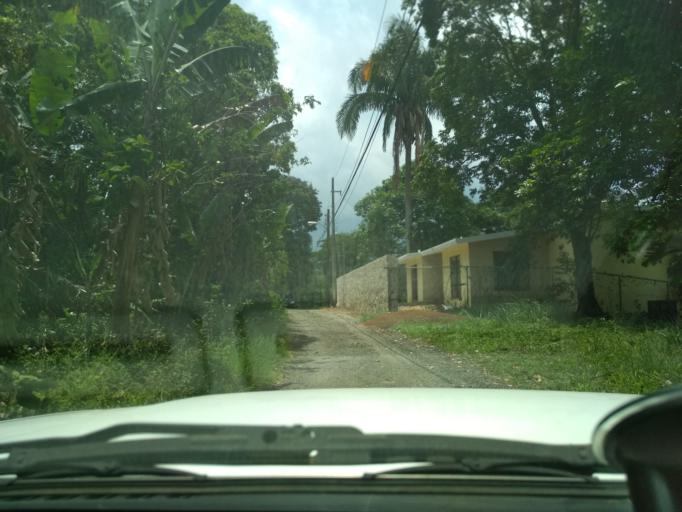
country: MX
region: Veracruz
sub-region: Cordoba
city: San Jose de Abajo [Unidad Habitacional]
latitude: 18.9188
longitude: -96.9573
